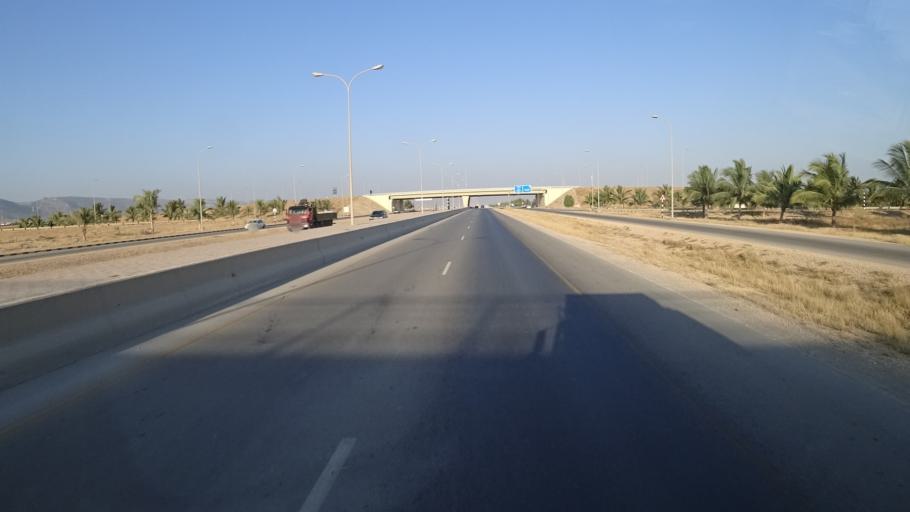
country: OM
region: Zufar
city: Salalah
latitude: 17.0583
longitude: 54.0812
